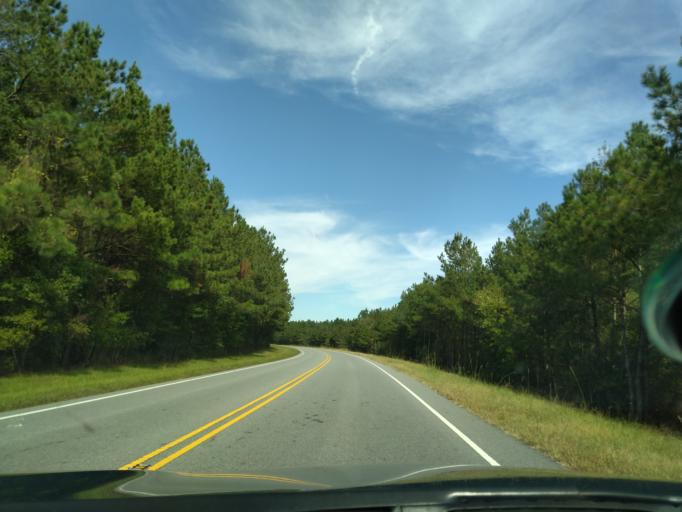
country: US
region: North Carolina
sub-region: Beaufort County
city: River Road
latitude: 35.5138
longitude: -76.8984
